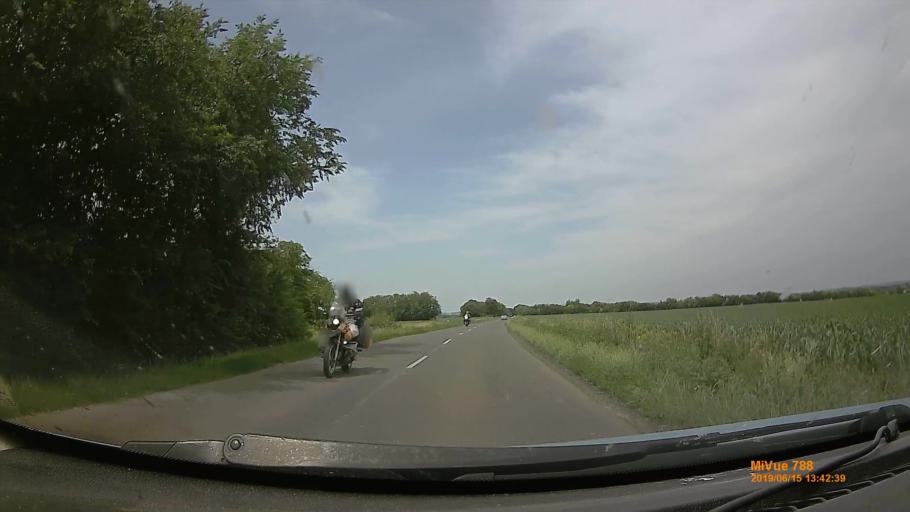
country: HU
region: Tolna
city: Iregszemcse
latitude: 46.6669
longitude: 18.1840
